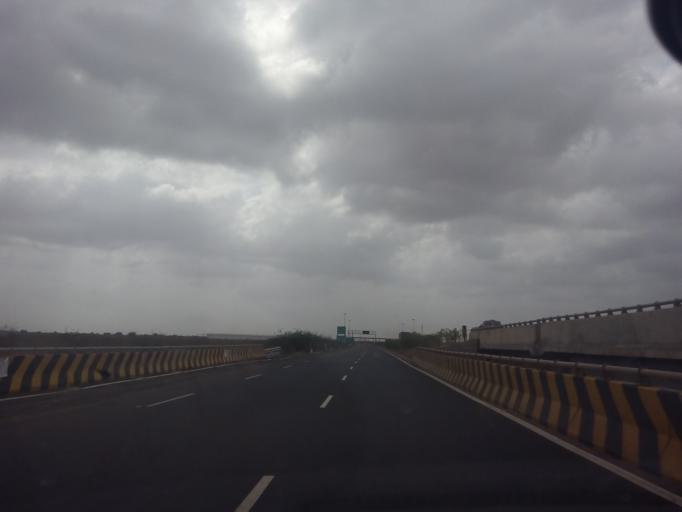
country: IN
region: Gujarat
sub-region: Rajkot
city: Morbi
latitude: 23.0389
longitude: 70.9214
